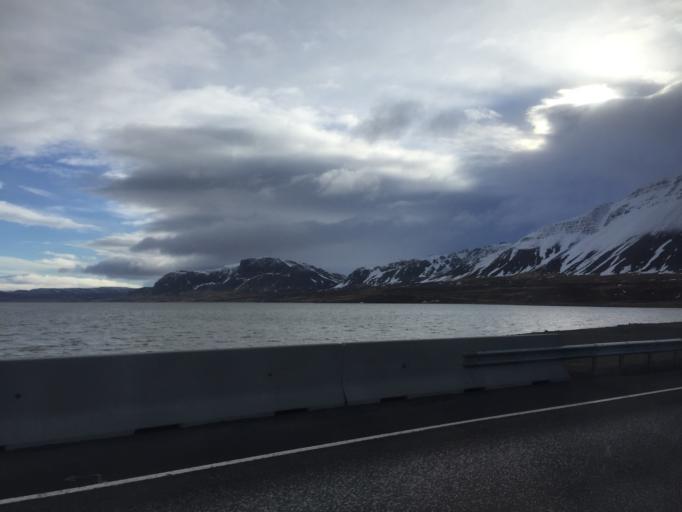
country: IS
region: West
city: Borgarnes
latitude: 64.5296
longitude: -21.8850
